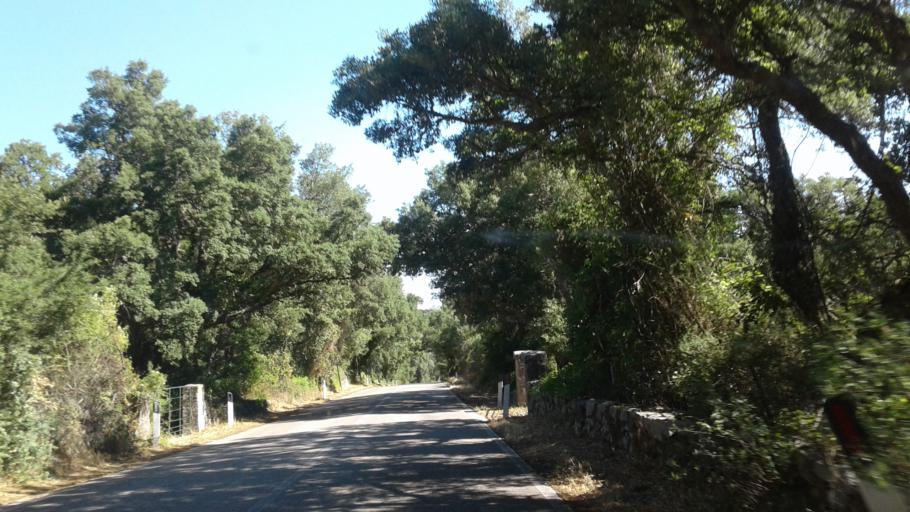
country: IT
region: Sardinia
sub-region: Provincia di Olbia-Tempio
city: Aggius
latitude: 40.9442
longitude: 9.0874
